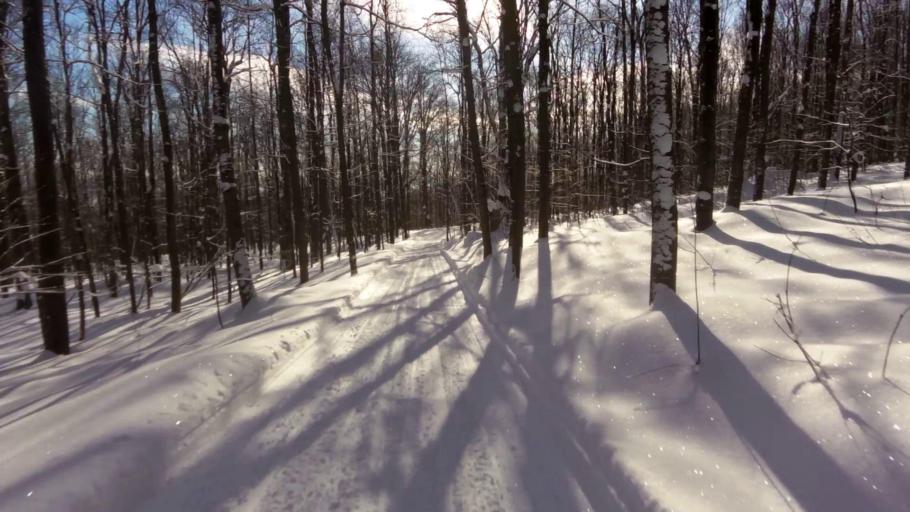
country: US
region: New York
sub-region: Chautauqua County
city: Falconer
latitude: 42.2757
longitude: -79.1243
